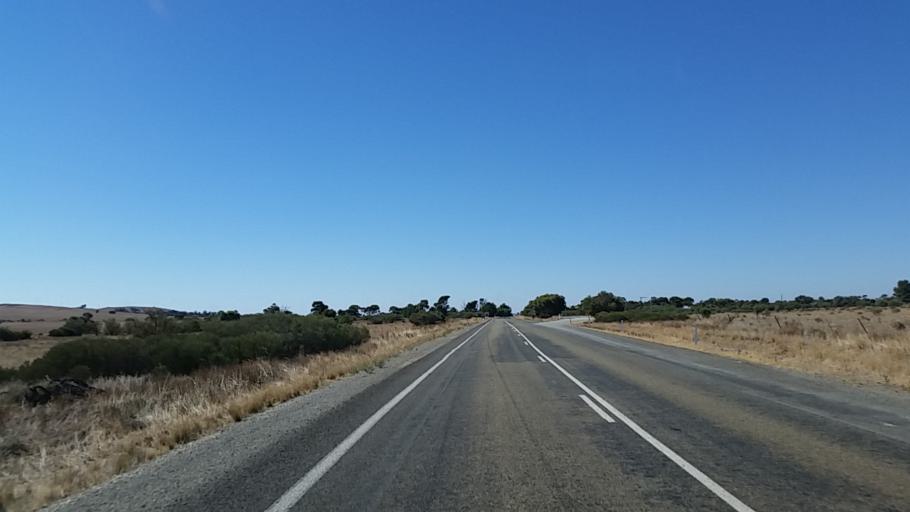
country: AU
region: South Australia
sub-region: Peterborough
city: Peterborough
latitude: -33.2325
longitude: 138.8794
